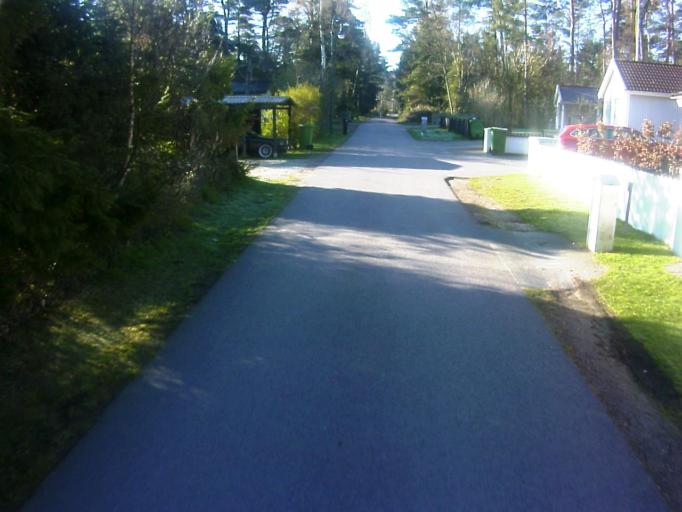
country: SE
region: Skane
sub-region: Kavlinge Kommun
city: Hofterup
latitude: 55.8174
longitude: 12.9711
